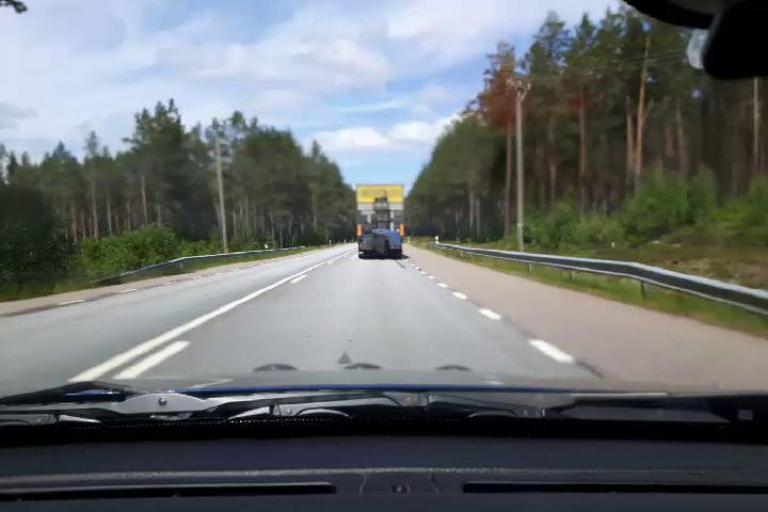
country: SE
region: Uppsala
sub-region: Tierps Kommun
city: Tierp
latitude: 60.1888
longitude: 17.4782
